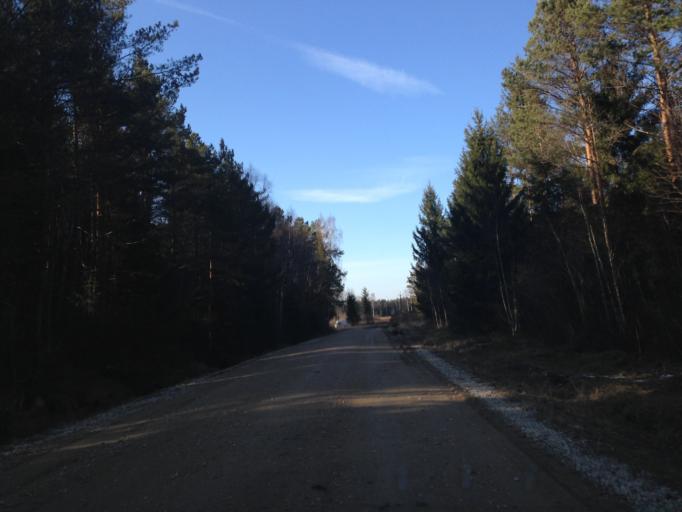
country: EE
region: Harju
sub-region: Nissi vald
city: Turba
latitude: 59.1578
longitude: 24.1440
